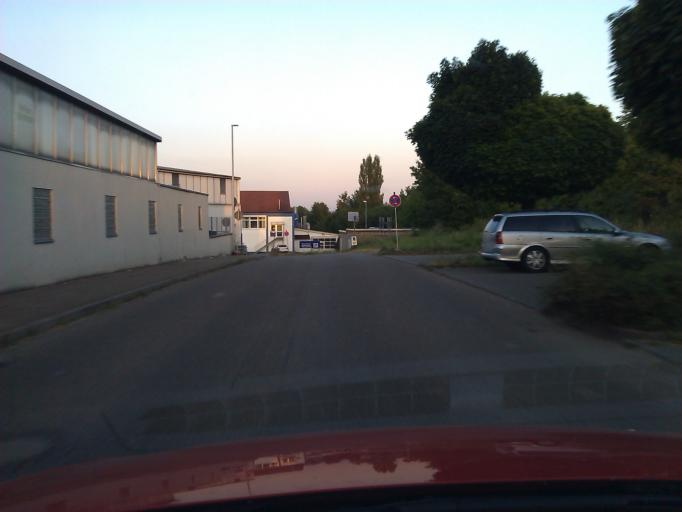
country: DE
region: Baden-Wuerttemberg
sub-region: Regierungsbezirk Stuttgart
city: Brackenheim
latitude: 49.0734
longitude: 9.0680
